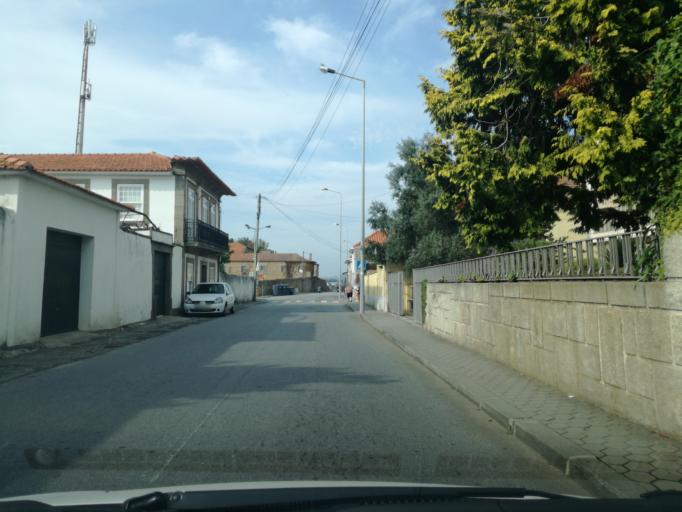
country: PT
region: Porto
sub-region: Vila Nova de Gaia
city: Arcozelo
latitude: 41.0512
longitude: -8.6274
